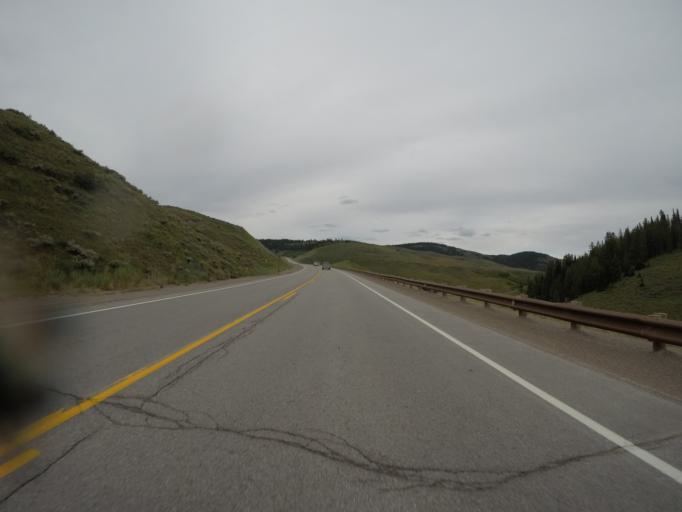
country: US
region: Wyoming
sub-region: Lincoln County
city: Afton
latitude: 42.4858
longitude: -110.9247
